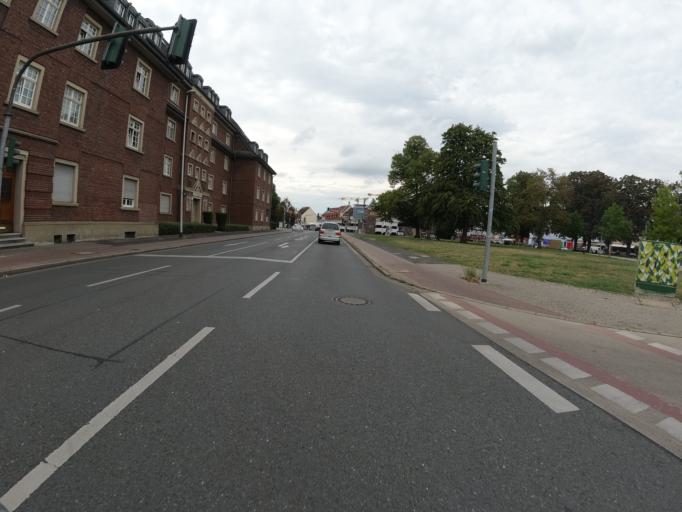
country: DE
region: North Rhine-Westphalia
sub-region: Regierungsbezirk Dusseldorf
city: Moers
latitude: 51.4491
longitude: 6.6403
